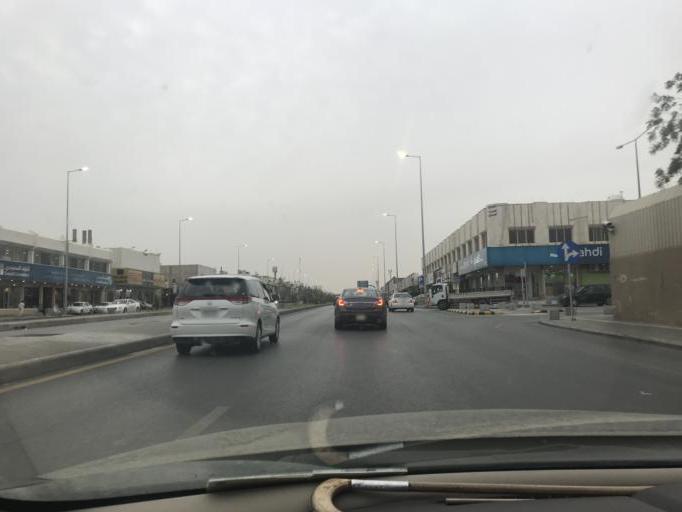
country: SA
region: Ar Riyad
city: Riyadh
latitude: 24.7584
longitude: 46.7669
